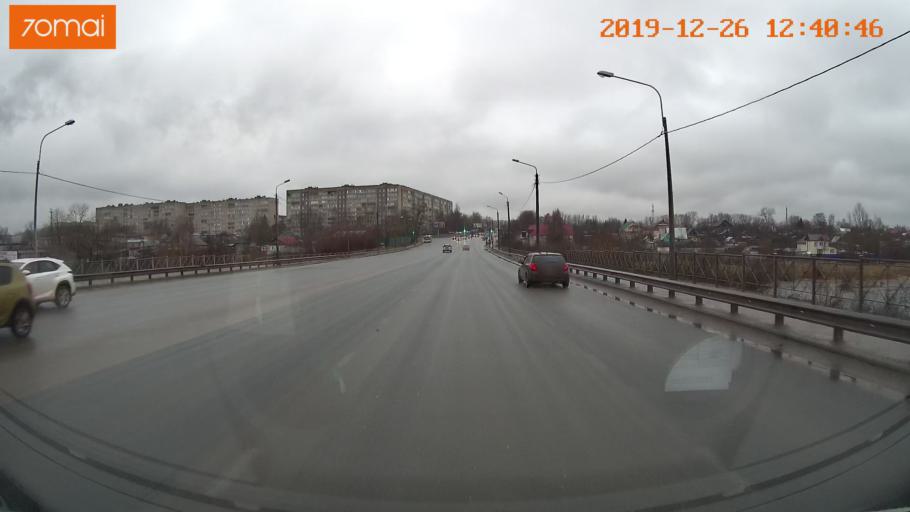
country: RU
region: Vologda
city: Tonshalovo
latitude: 59.1441
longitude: 37.9687
